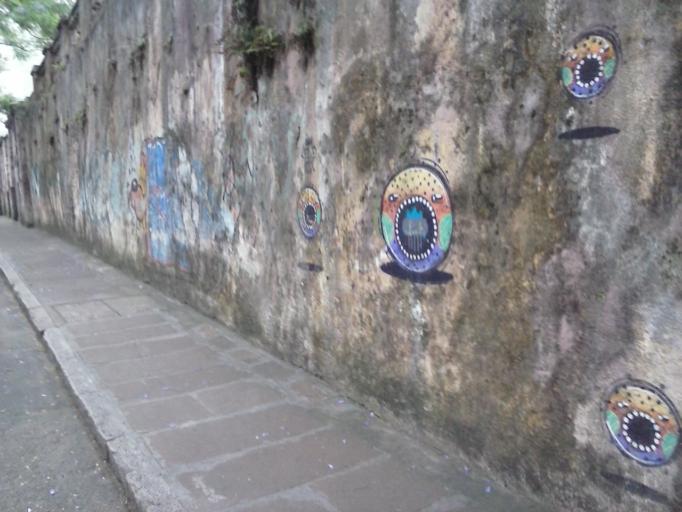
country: BR
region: Rio Grande do Sul
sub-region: Porto Alegre
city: Porto Alegre
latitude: -30.0337
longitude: -51.2327
